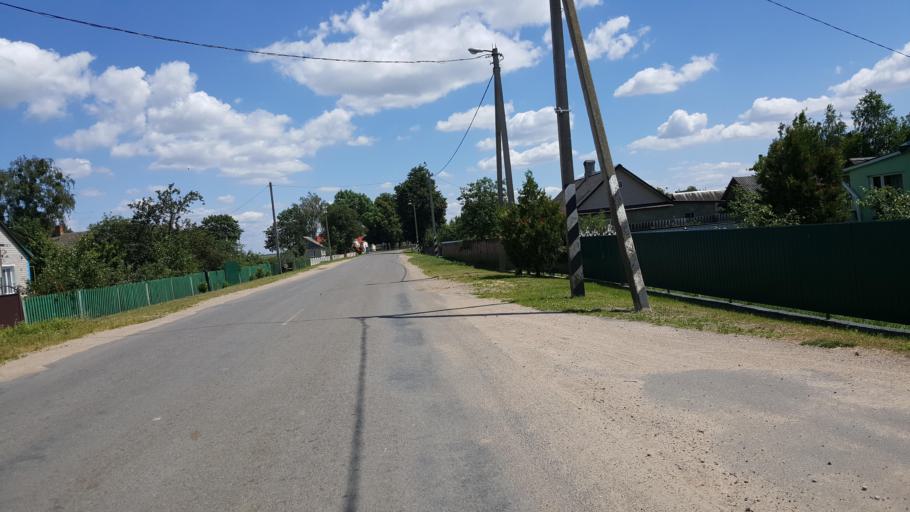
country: PL
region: Podlasie
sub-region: Powiat hajnowski
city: Czeremcha
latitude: 52.4895
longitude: 23.4483
